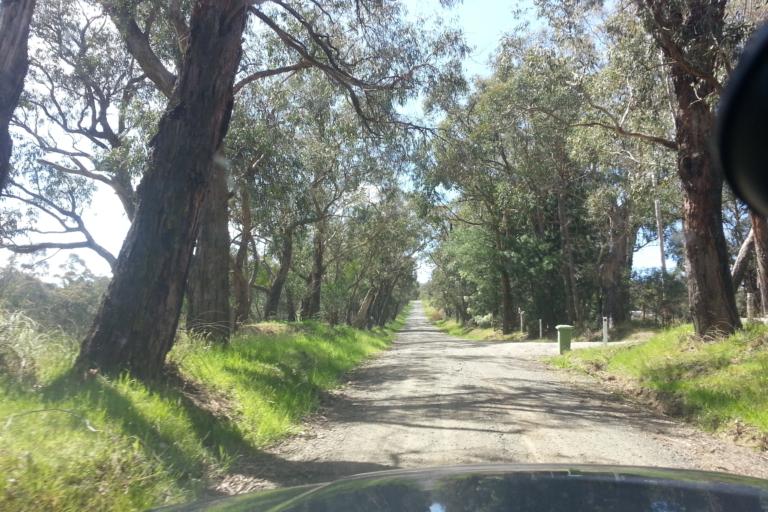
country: AU
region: Victoria
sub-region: Cardinia
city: Beaconsfield Upper
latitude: -37.9858
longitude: 145.3819
